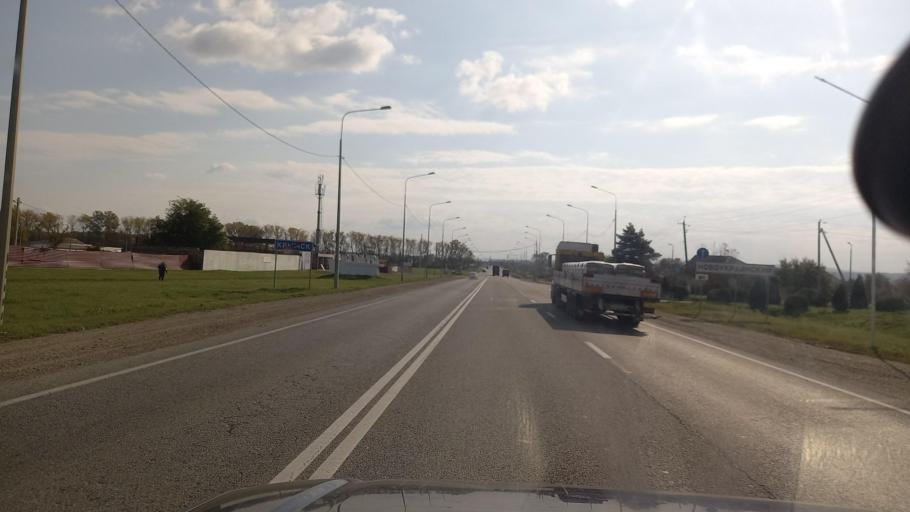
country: RU
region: Krasnodarskiy
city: Novoukrainskiy
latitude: 44.9043
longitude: 38.0311
